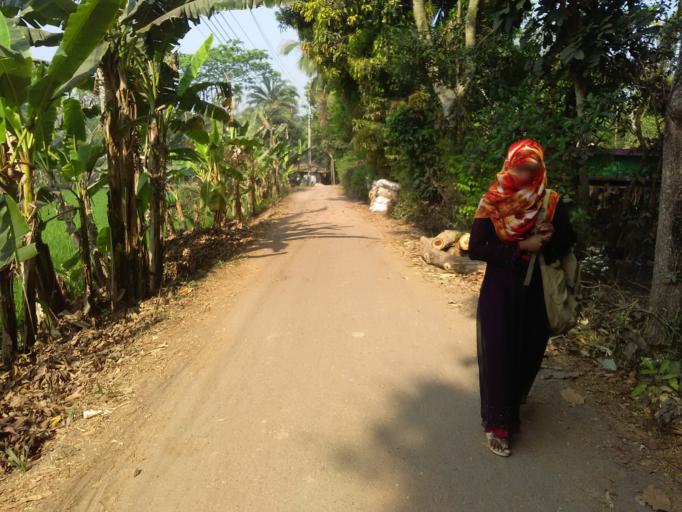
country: BD
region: Khulna
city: Khulna
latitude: 22.8966
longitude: 89.5309
